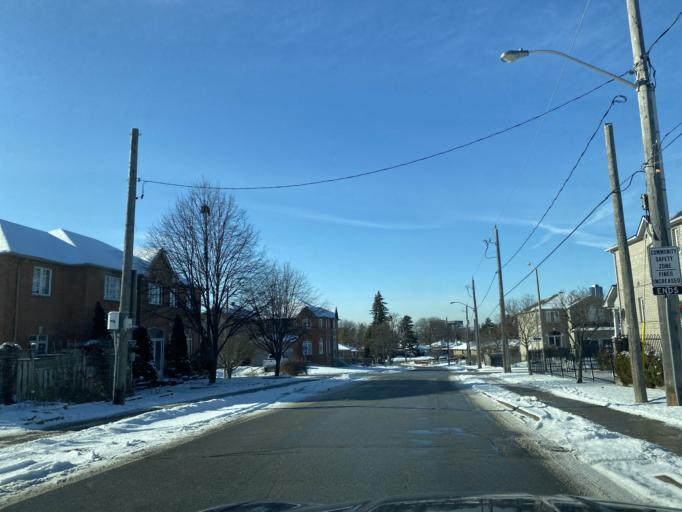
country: CA
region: Ontario
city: Scarborough
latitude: 43.7733
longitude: -79.3099
